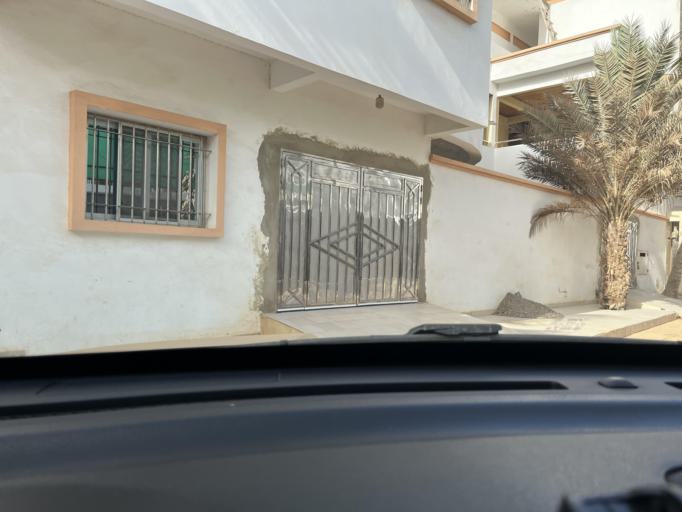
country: SN
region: Dakar
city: Mermoz Boabab
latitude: 14.7473
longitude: -17.5201
